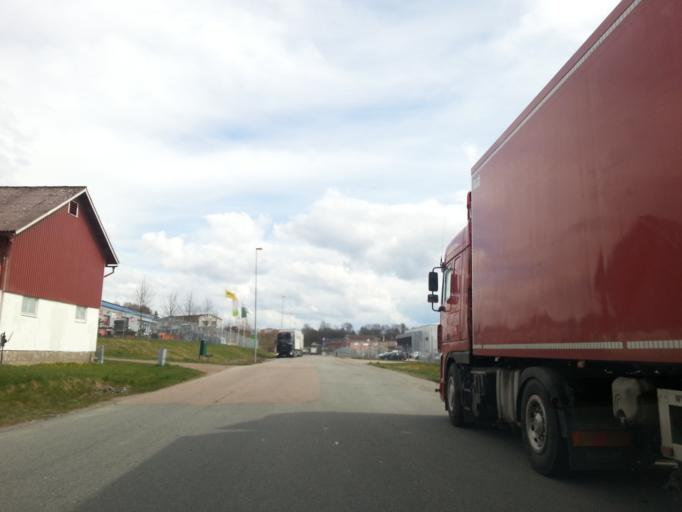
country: SE
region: Vaestra Goetaland
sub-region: Kungalvs Kommun
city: Kungalv
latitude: 57.8786
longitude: 11.9257
